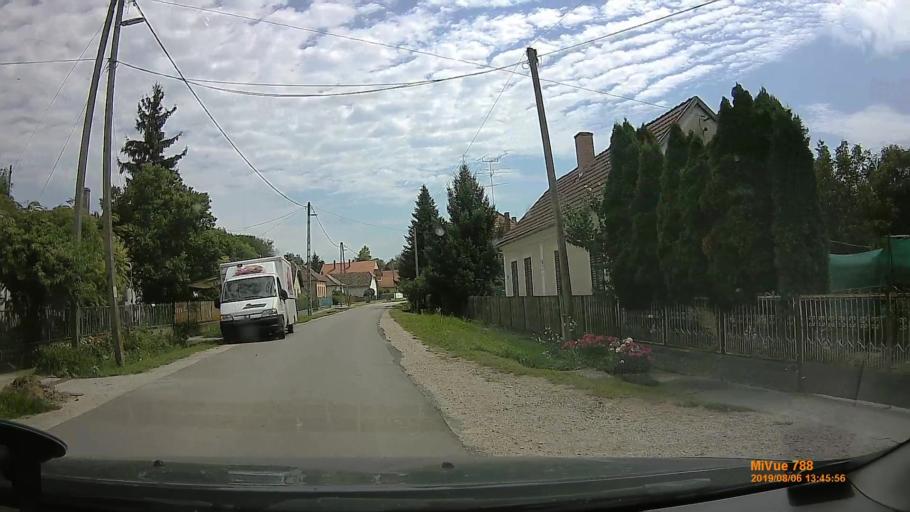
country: HU
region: Zala
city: Zalakomar
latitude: 46.5742
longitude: 17.0967
